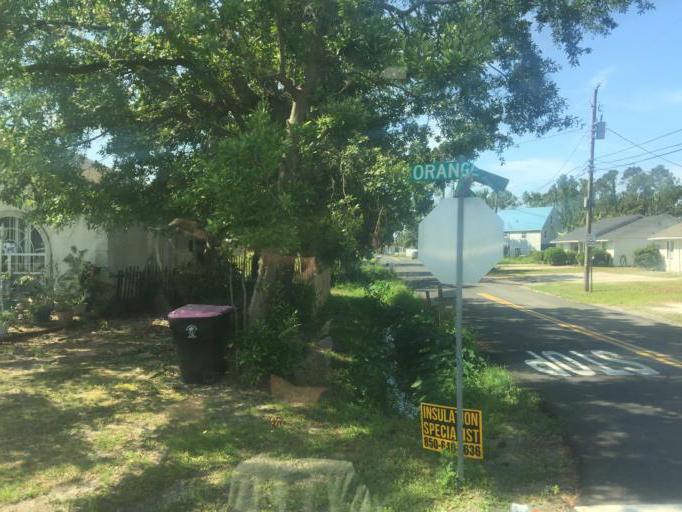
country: US
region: Florida
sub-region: Bay County
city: Lower Grand Lagoon
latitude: 30.1558
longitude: -85.7535
